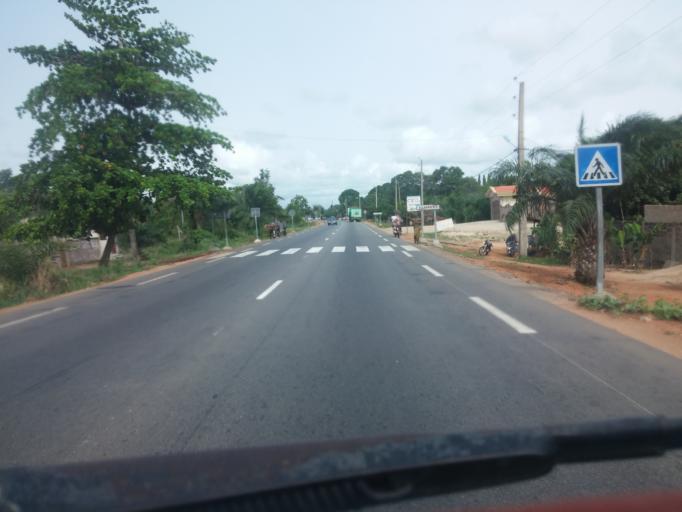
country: BJ
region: Mono
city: Come
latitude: 6.4004
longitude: 1.9191
